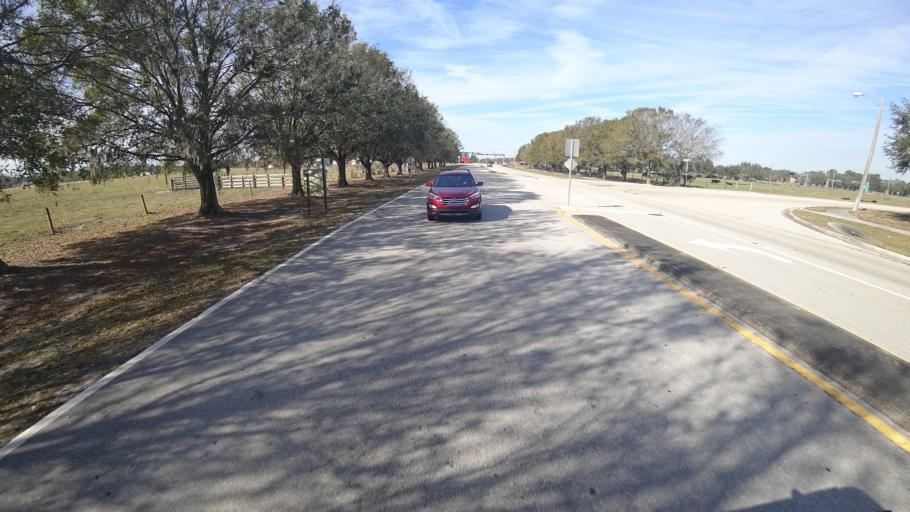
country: US
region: Florida
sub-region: Manatee County
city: Memphis
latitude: 27.5792
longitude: -82.5382
